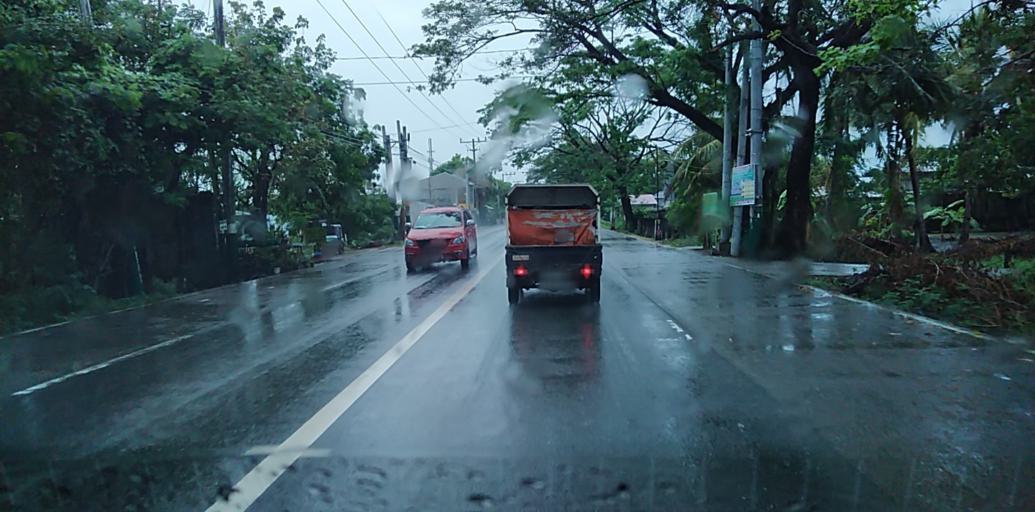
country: PH
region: Central Luzon
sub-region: Province of Bulacan
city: Bulualto
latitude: 15.2179
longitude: 120.9545
